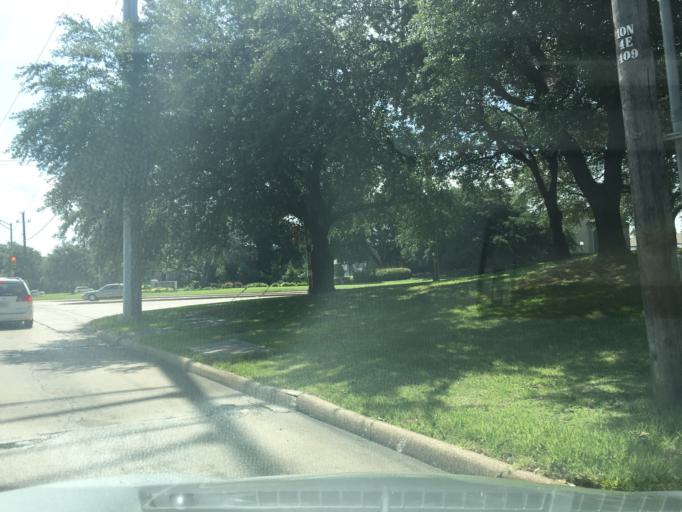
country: US
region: Texas
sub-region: Dallas County
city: Richardson
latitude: 32.9231
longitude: -96.7404
